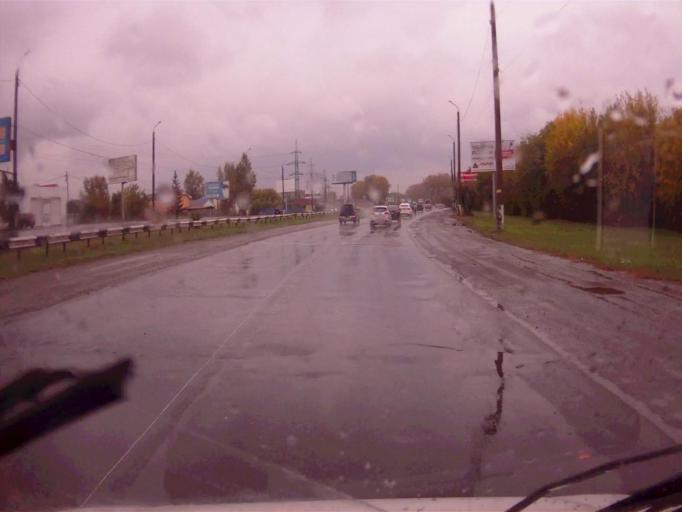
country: RU
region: Chelyabinsk
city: Dolgoderevenskoye
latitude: 55.2381
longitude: 61.3615
